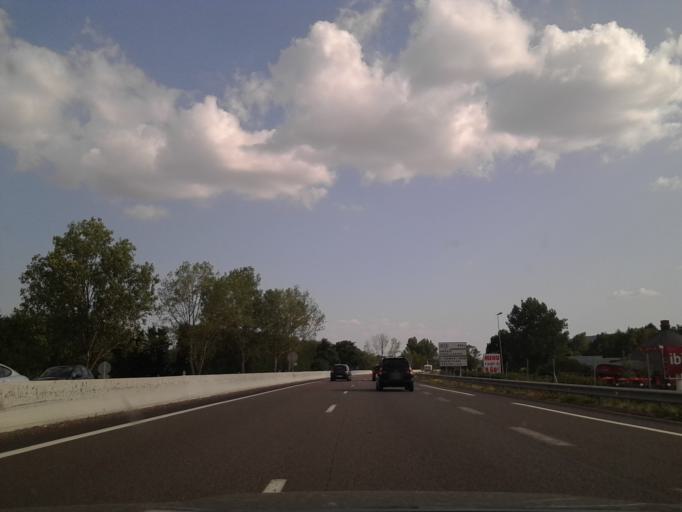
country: FR
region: Auvergne
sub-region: Departement du Puy-de-Dome
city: Issoire
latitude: 45.5488
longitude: 3.2691
